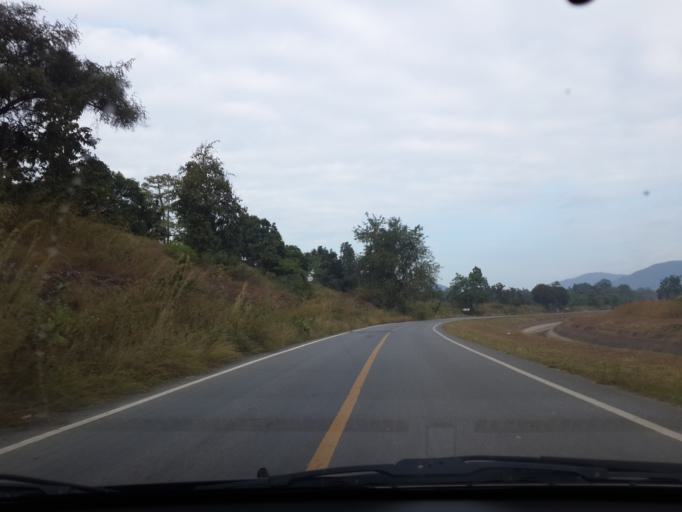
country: TH
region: Chiang Mai
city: San Sai
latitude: 18.8965
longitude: 99.1490
